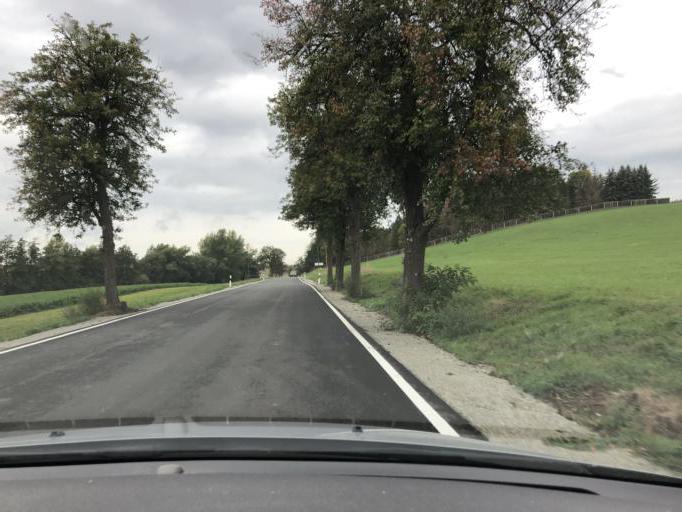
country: DE
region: Saxony-Anhalt
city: Uichteritz
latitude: 51.2111
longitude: 11.9092
